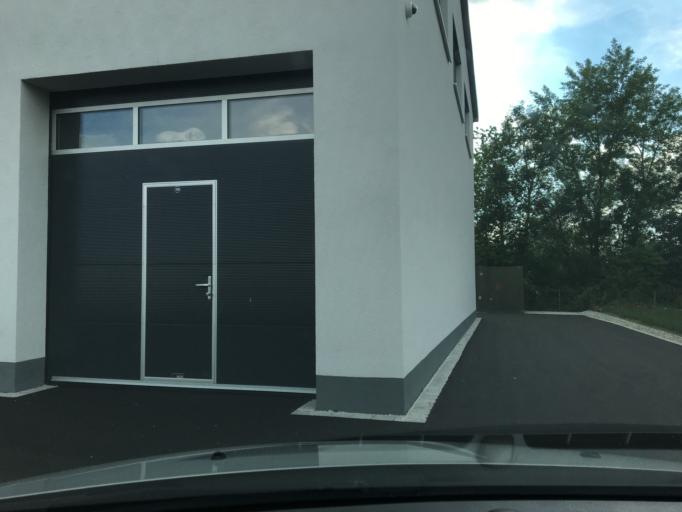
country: DE
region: Bavaria
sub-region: Lower Bavaria
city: Bruckberg
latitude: 48.4838
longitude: 12.0145
